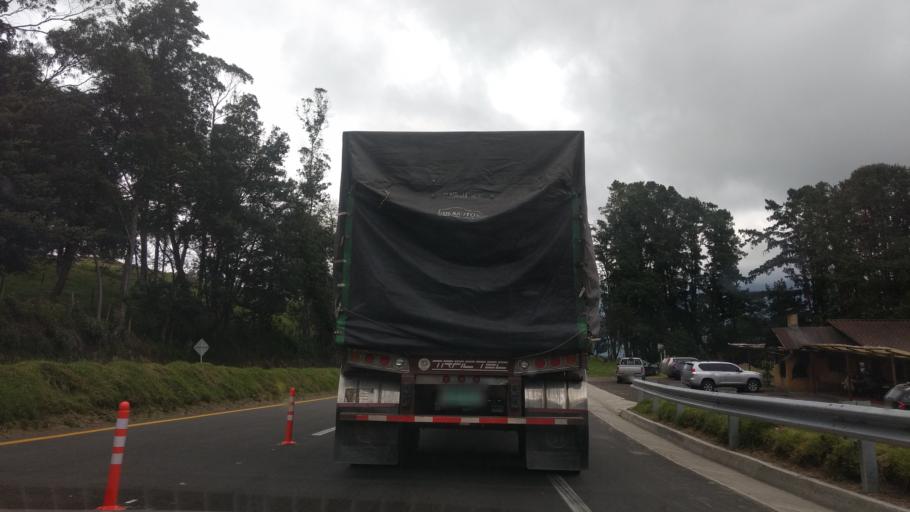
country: CO
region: Cundinamarca
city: San Francisco
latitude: 4.9204
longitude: -74.2925
